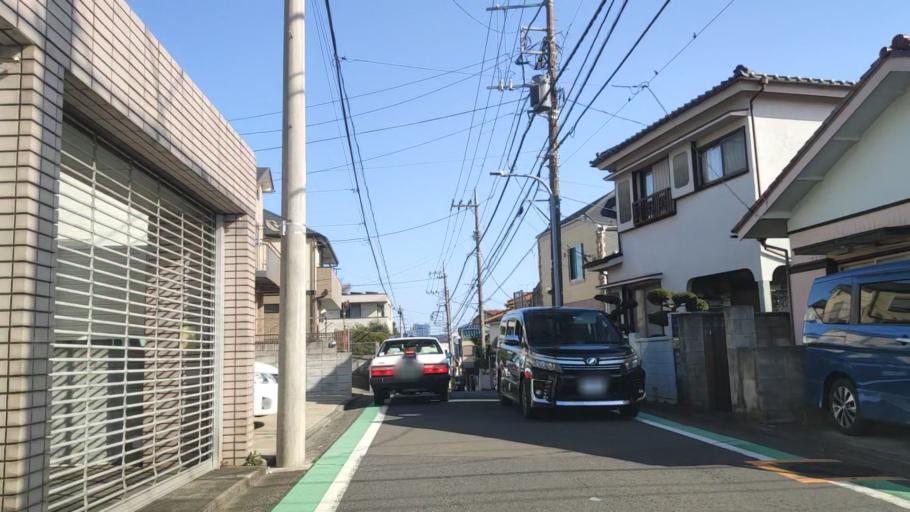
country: JP
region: Kanagawa
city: Yokohama
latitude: 35.4630
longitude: 139.6007
